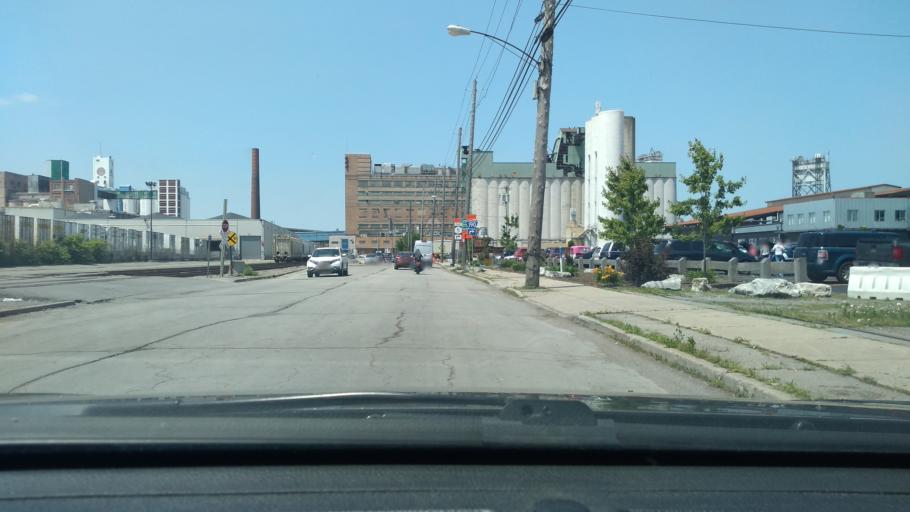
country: US
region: New York
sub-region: Erie County
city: Buffalo
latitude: 42.8685
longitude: -78.8731
